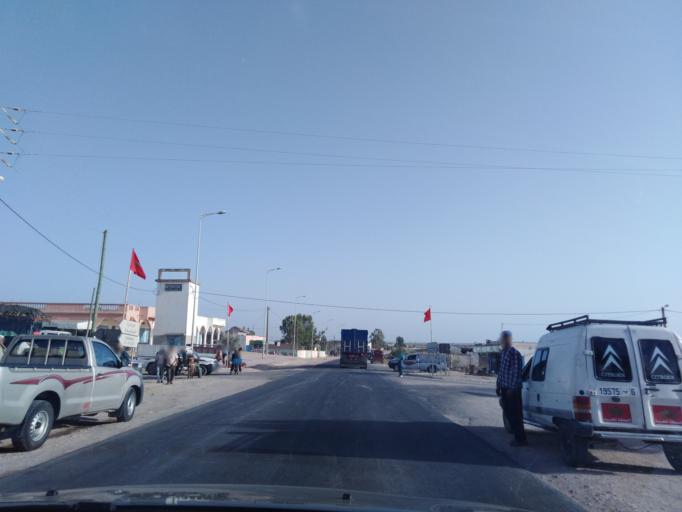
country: MA
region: Doukkala-Abda
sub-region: El-Jadida
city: Sidi Bennour
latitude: 32.5485
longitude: -8.7252
